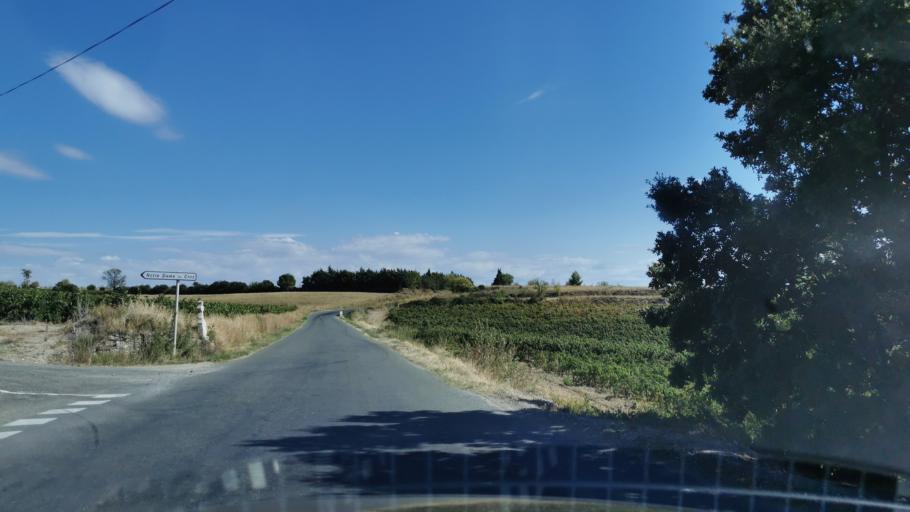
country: FR
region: Languedoc-Roussillon
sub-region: Departement de l'Aude
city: Caunes-Minervois
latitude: 43.3230
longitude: 2.5359
